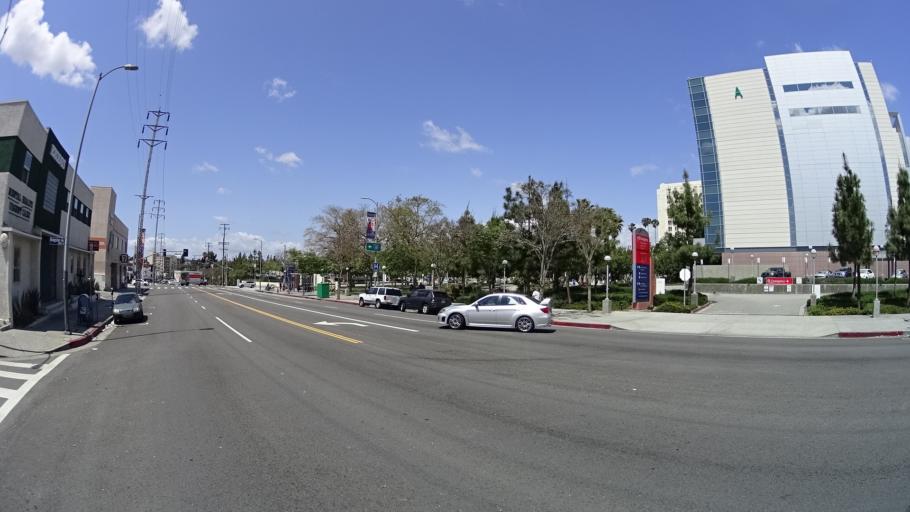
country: US
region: California
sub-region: Los Angeles County
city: Boyle Heights
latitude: 34.0573
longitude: -118.2092
